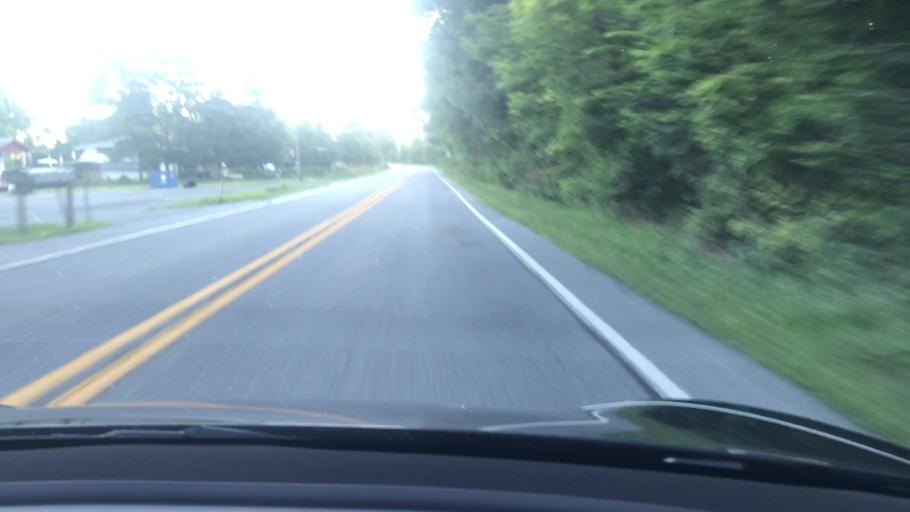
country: US
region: Pennsylvania
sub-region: York County
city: Dover
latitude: 40.0735
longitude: -76.8787
